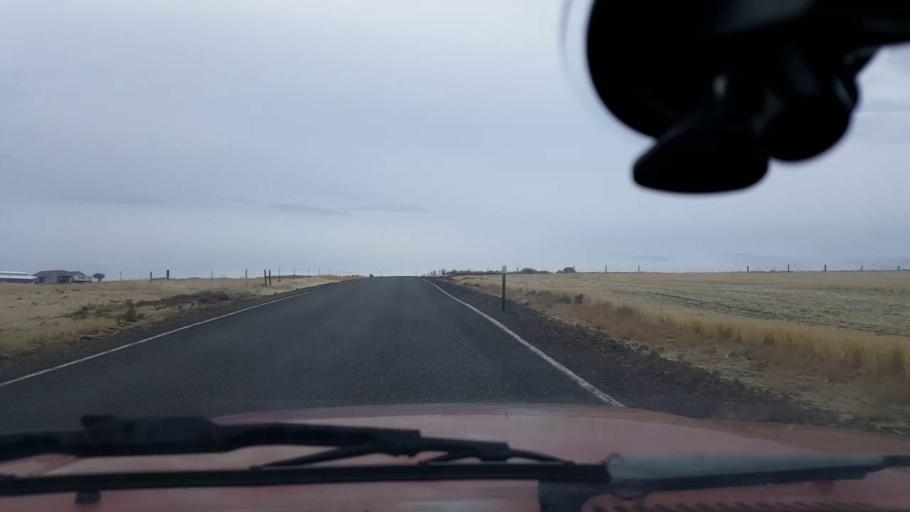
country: US
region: Washington
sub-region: Asotin County
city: Clarkston Heights-Vineland
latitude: 46.3408
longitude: -117.2713
